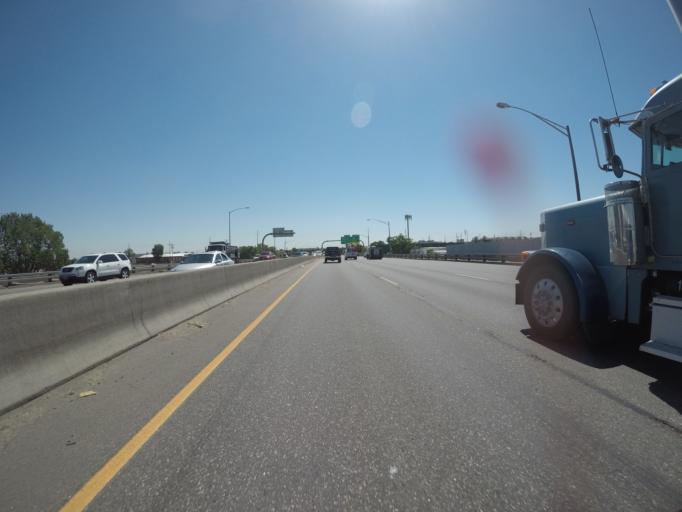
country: US
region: Colorado
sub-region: Adams County
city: Commerce City
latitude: 39.7799
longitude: -104.9452
